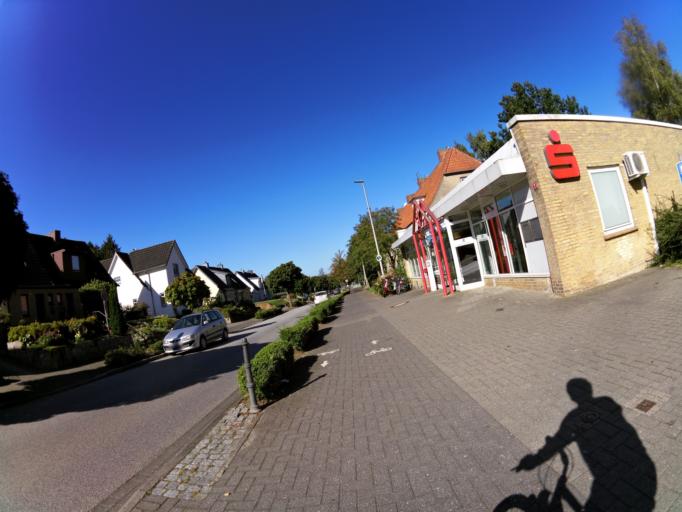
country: DE
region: Schleswig-Holstein
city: Eckernforde
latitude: 54.4823
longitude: 9.8328
